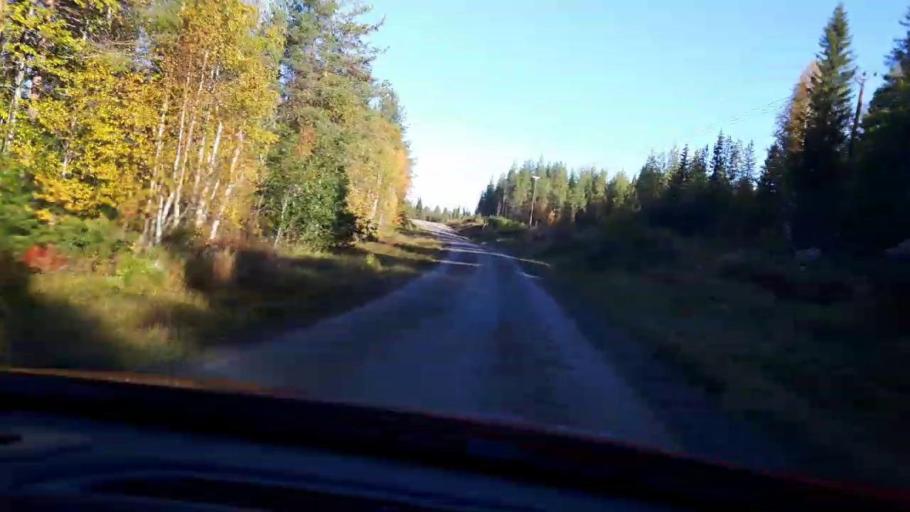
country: SE
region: Jaemtland
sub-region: Stroemsunds Kommun
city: Stroemsund
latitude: 64.3719
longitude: 15.1556
